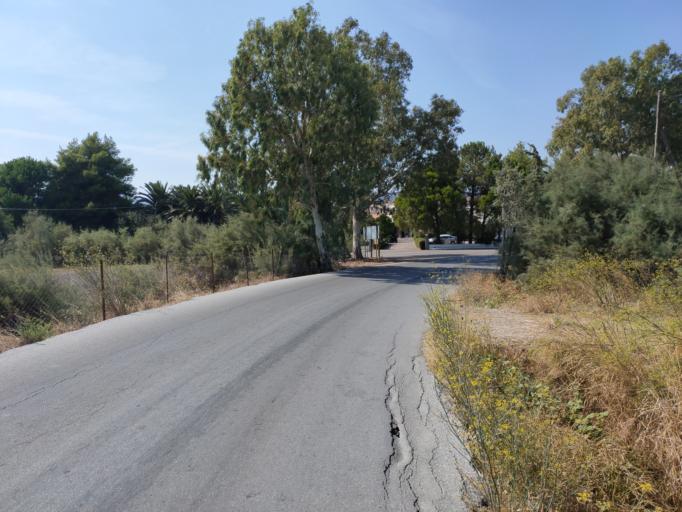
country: GR
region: North Aegean
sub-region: Nomos Lesvou
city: Kalloni
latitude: 39.2092
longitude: 26.2073
